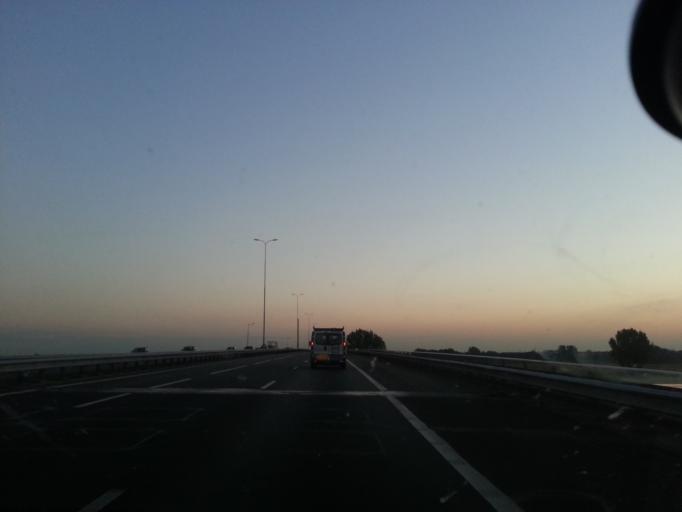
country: NL
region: Utrecht
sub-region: Gemeente Vianen
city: Vianen
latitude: 52.0038
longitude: 5.1152
